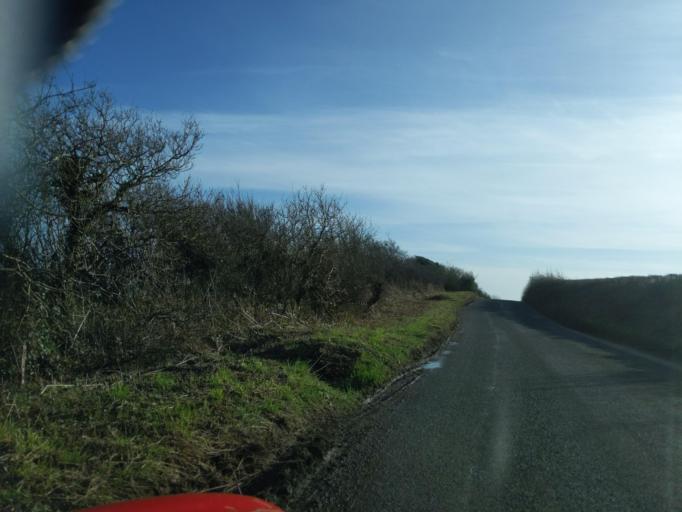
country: GB
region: England
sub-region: Devon
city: Kingsbridge
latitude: 50.3474
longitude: -3.7274
